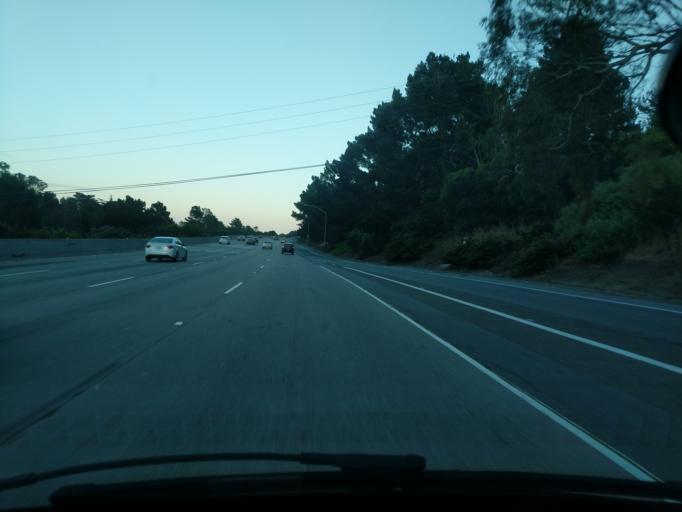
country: US
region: California
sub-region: San Mateo County
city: Colma
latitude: 37.6442
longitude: -122.4483
